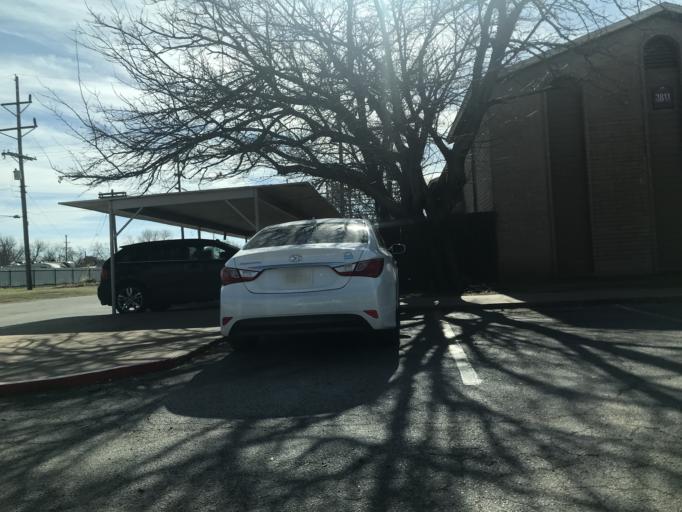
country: US
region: Texas
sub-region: Taylor County
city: Abilene
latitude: 32.4186
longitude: -99.7567
